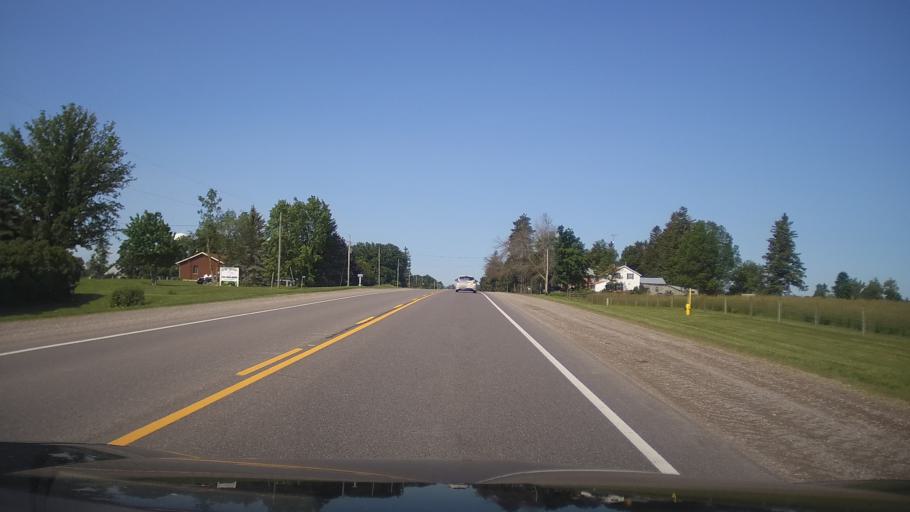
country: CA
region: Ontario
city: Omemee
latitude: 44.3417
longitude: -78.8404
